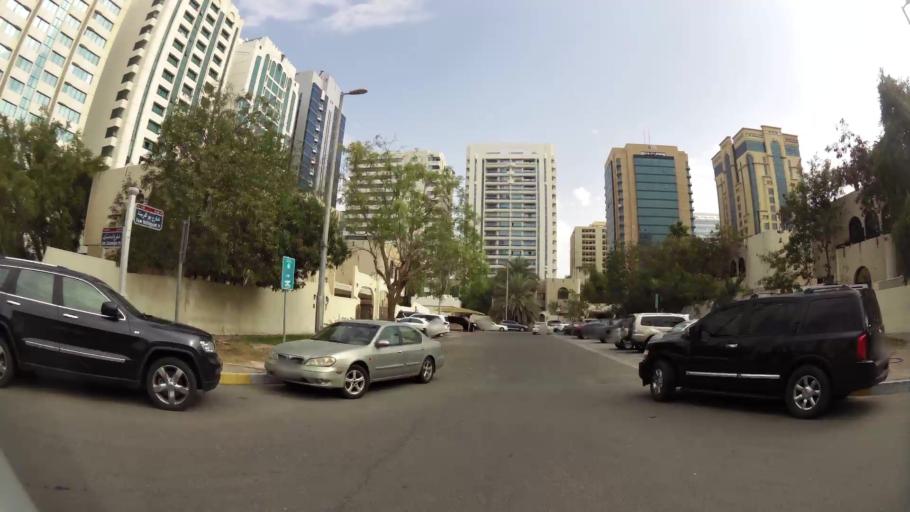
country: AE
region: Abu Dhabi
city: Abu Dhabi
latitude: 24.4807
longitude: 54.3536
